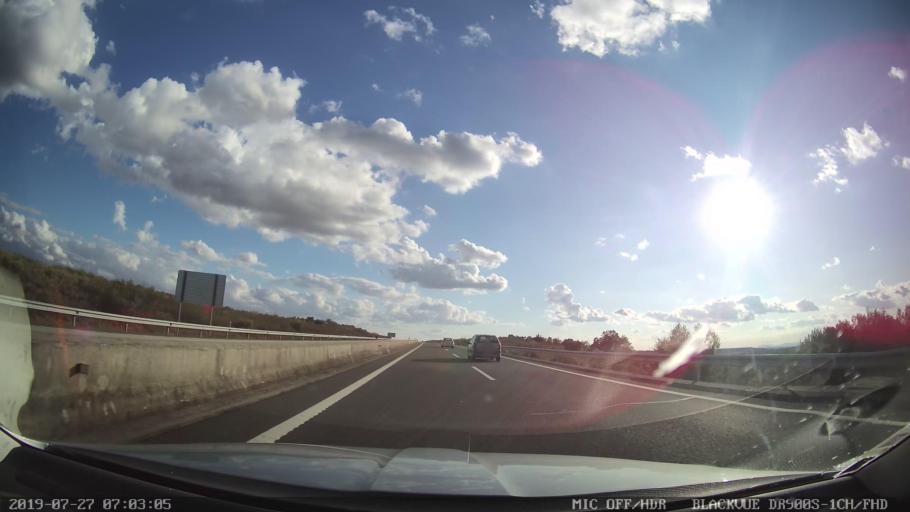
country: ES
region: Extremadura
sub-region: Provincia de Caceres
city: Casas de Miravete
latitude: 39.6803
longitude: -5.7319
